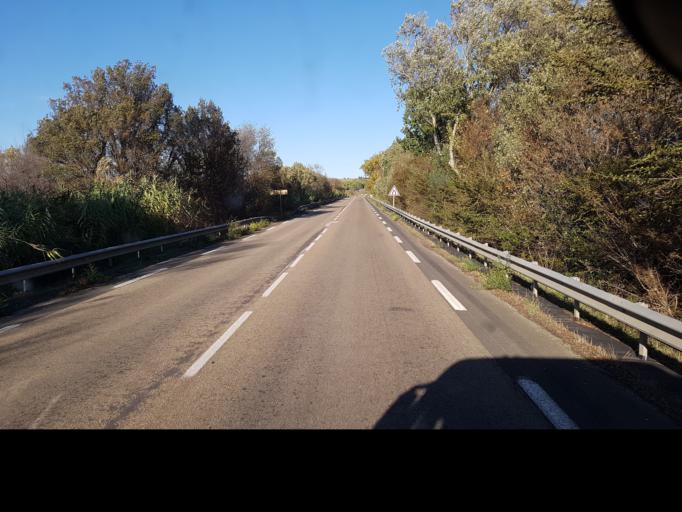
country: FR
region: Languedoc-Roussillon
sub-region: Departement de l'Aude
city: Coursan
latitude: 43.2583
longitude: 3.0753
